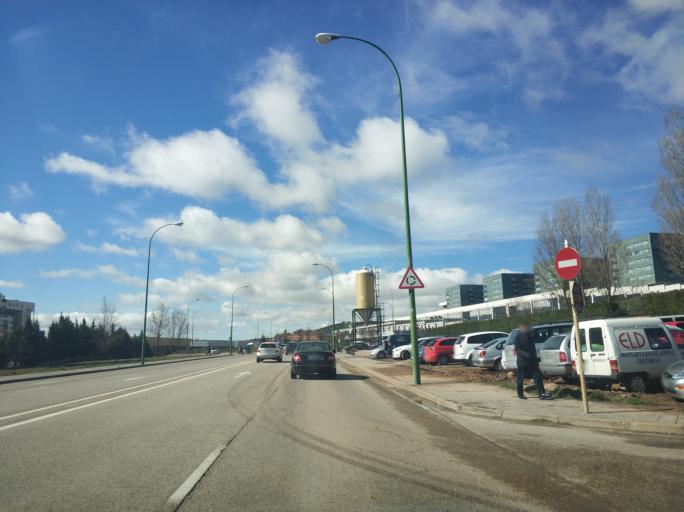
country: ES
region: Castille and Leon
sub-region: Provincia de Burgos
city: Burgos
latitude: 42.3632
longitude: -3.6805
